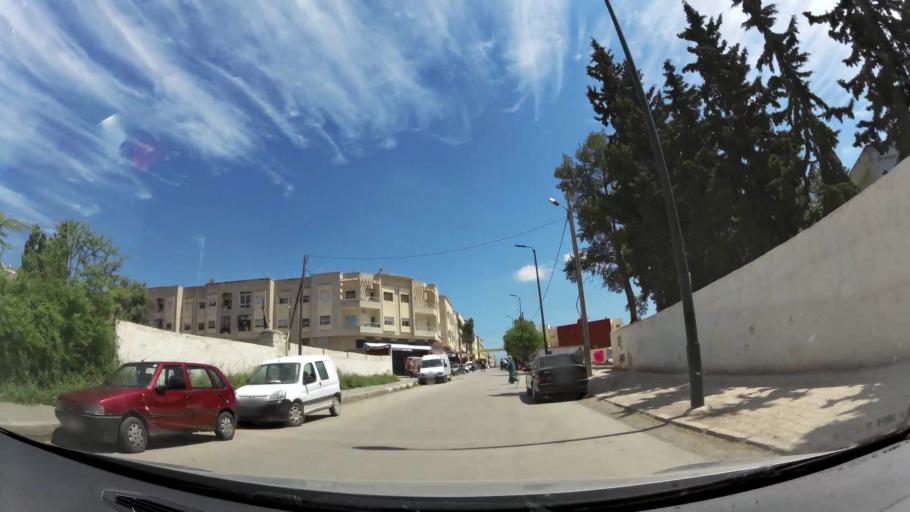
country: MA
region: Fes-Boulemane
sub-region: Fes
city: Fes
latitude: 34.0102
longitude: -4.9829
